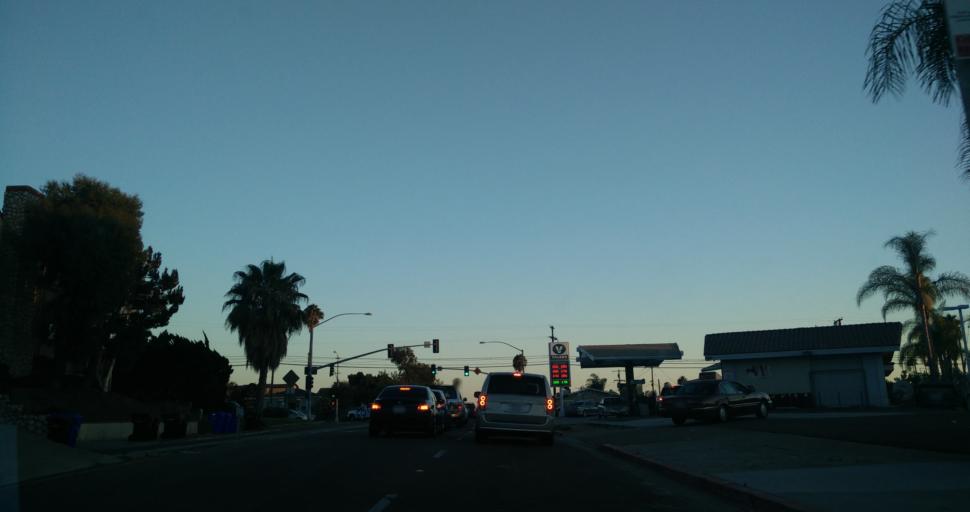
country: US
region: California
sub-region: San Diego County
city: San Diego
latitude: 32.7619
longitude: -117.1389
